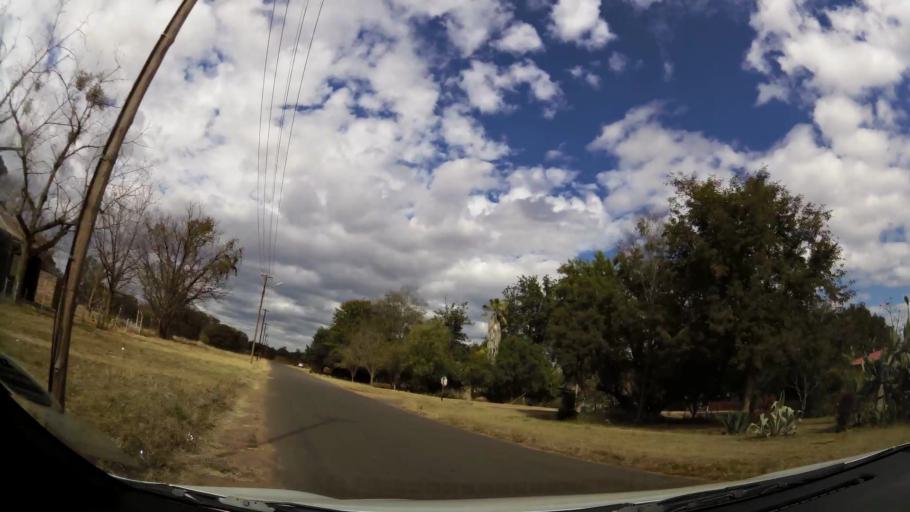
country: ZA
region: Limpopo
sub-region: Waterberg District Municipality
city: Modimolle
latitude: -24.7080
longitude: 28.4093
